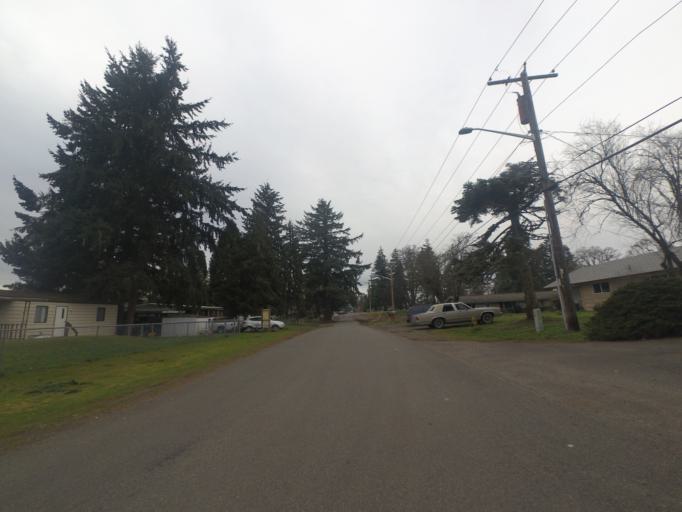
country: US
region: Washington
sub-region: Pierce County
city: McChord Air Force Base
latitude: 47.1249
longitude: -122.5259
